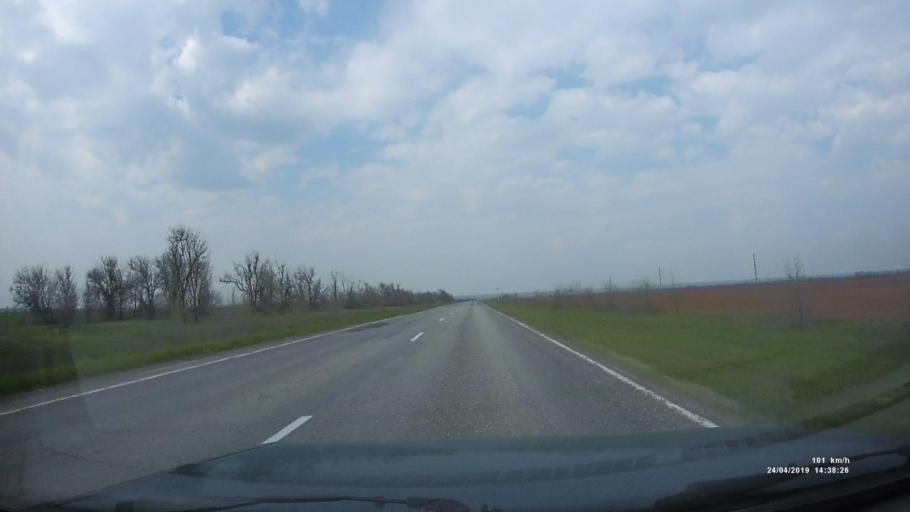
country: RU
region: Rostov
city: Remontnoye
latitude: 46.4013
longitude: 43.8861
